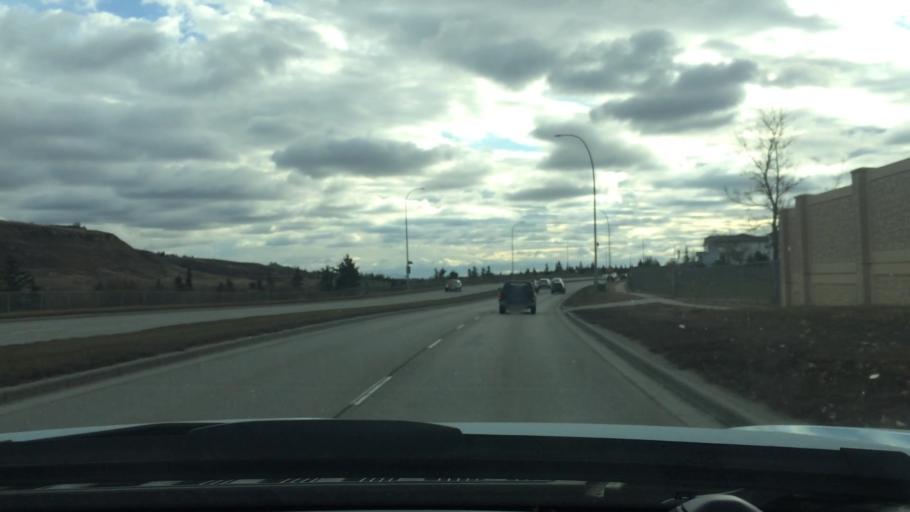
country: CA
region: Alberta
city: Calgary
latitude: 51.1516
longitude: -114.1008
